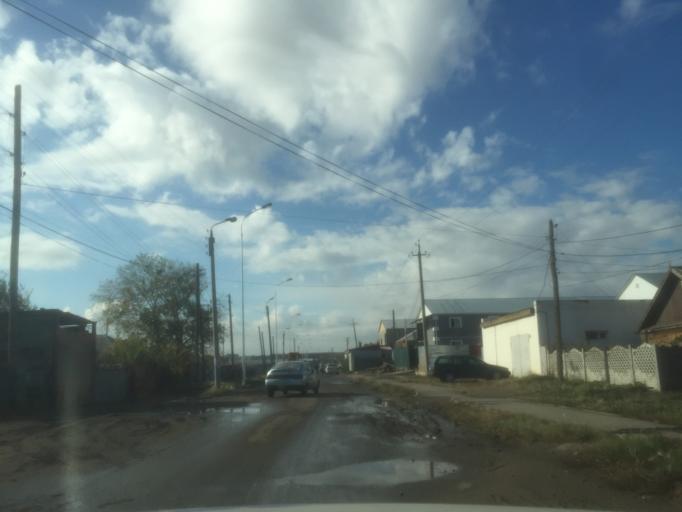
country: KZ
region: Astana Qalasy
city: Astana
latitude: 51.1856
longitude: 71.3915
